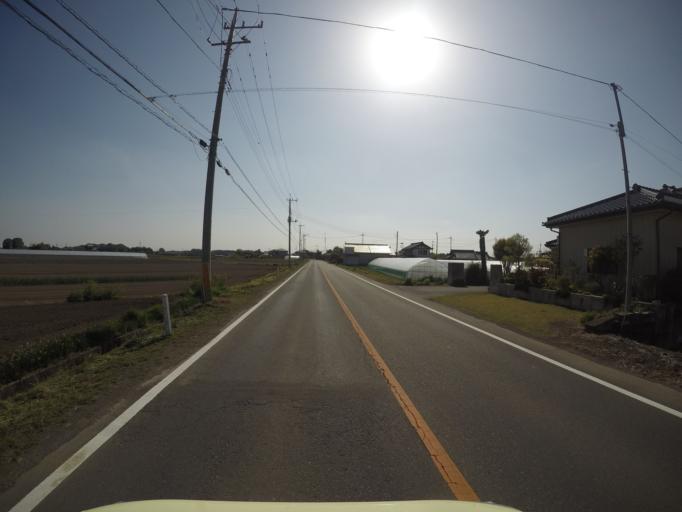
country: JP
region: Ibaraki
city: Yuki
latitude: 36.3598
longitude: 139.8991
